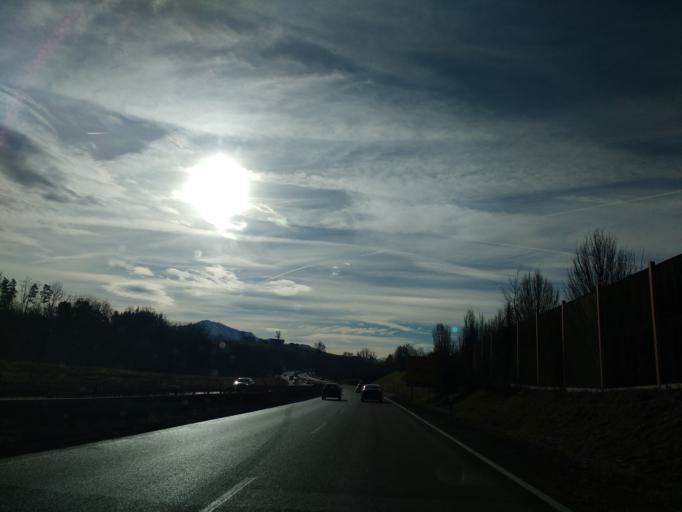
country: DE
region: Bavaria
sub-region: Swabia
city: Waltenhofen
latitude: 47.6624
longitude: 10.2988
